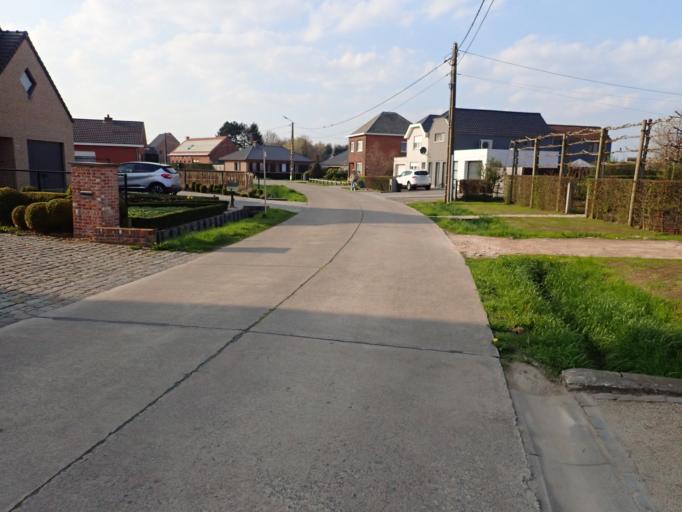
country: BE
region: Flanders
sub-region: Provincie Antwerpen
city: Berlaar
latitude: 51.0935
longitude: 4.6761
